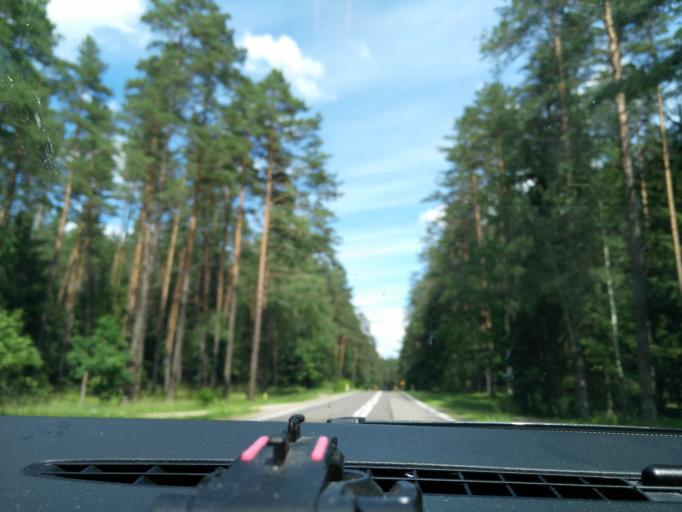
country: PL
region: Podlasie
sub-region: Powiat sejnenski
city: Krasnopol
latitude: 53.9719
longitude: 23.2574
